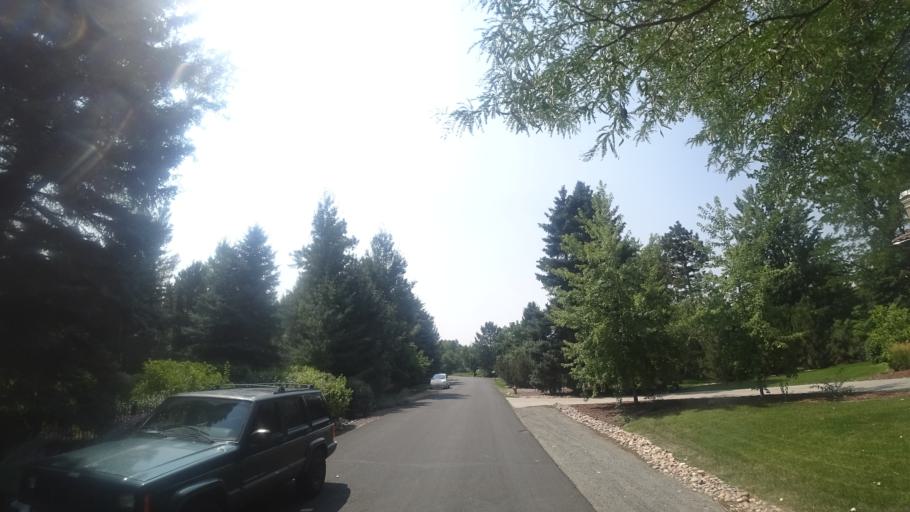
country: US
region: Colorado
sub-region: Arapahoe County
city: Cherry Hills Village
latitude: 39.6256
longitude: -104.9728
